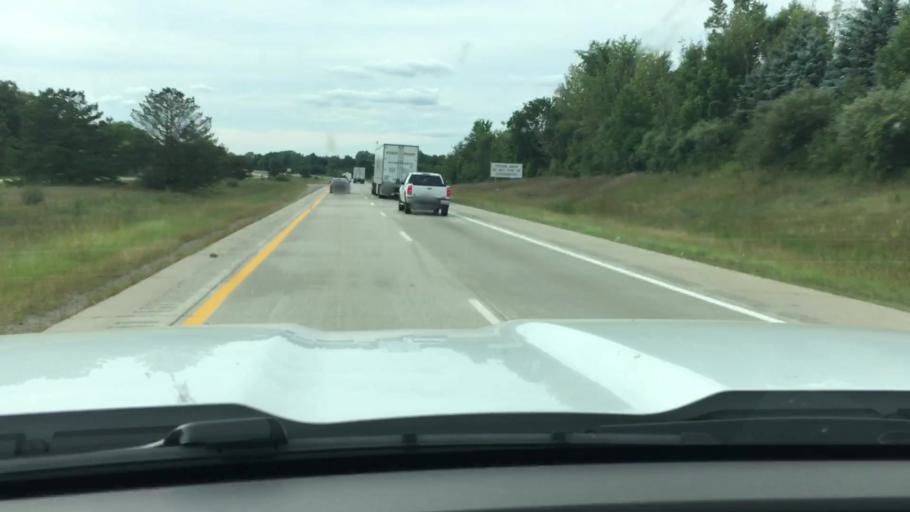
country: US
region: Michigan
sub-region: Lapeer County
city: Lapeer
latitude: 43.0282
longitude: -83.3388
